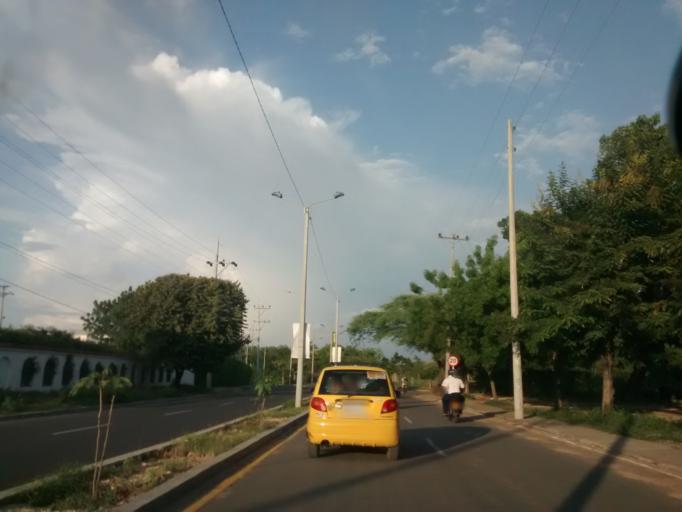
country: CO
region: Cundinamarca
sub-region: Girardot
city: Girardot City
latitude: 4.3060
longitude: -74.8126
